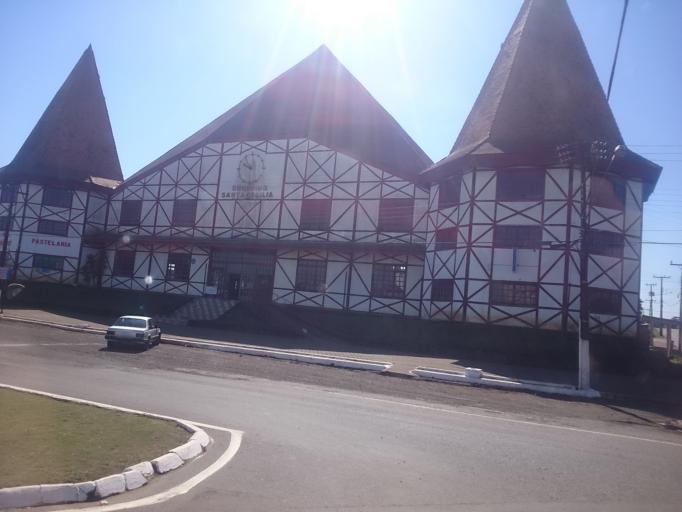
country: BR
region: Santa Catarina
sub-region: Santa Cecilia
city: Santa Cecilia
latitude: -26.9595
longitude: -50.4166
